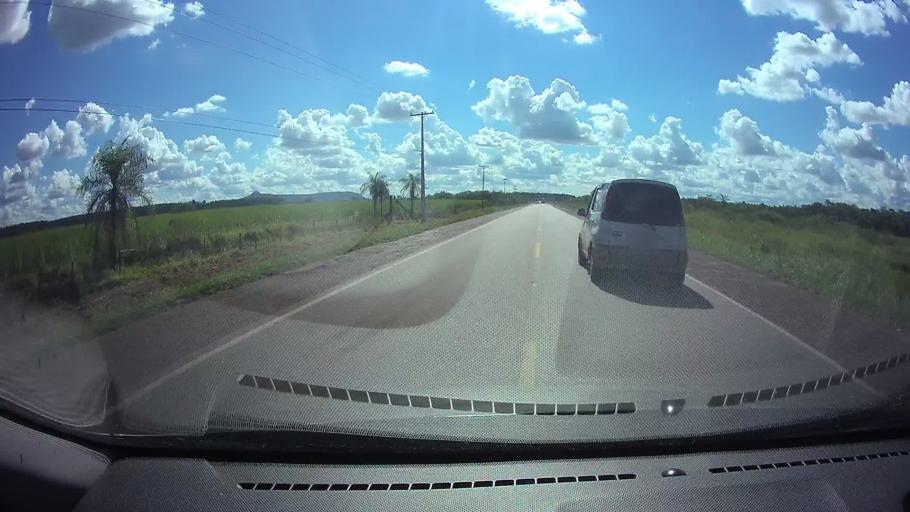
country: PY
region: Guaira
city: Coronel Martinez
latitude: -25.7624
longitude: -56.6894
